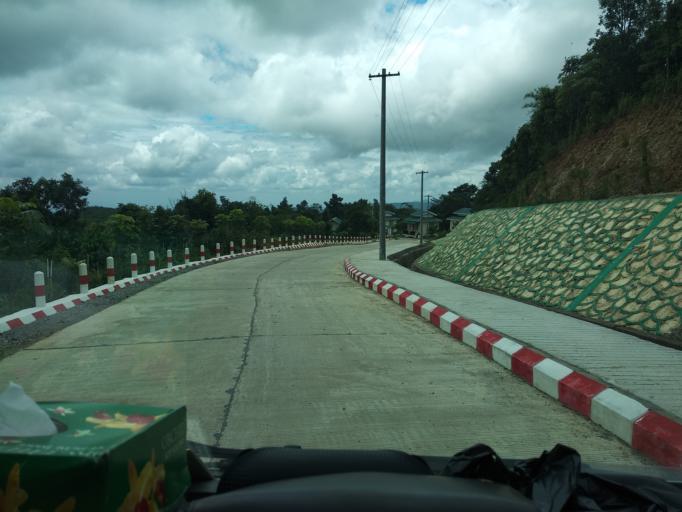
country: MM
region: Mandalay
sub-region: Pyin Oo Lwin District
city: Pyin Oo Lwin
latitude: 21.9103
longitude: 96.3871
